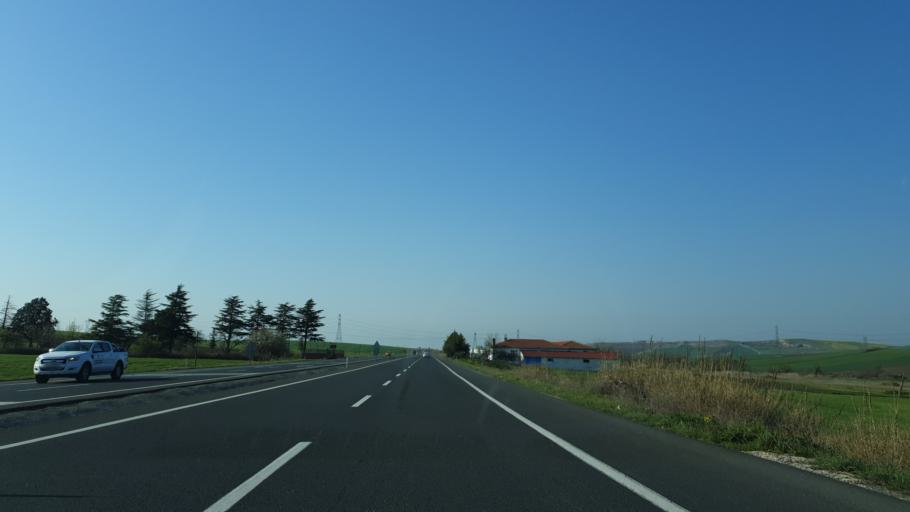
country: TR
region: Tekirdag
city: Corlu
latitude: 41.0838
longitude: 27.7424
